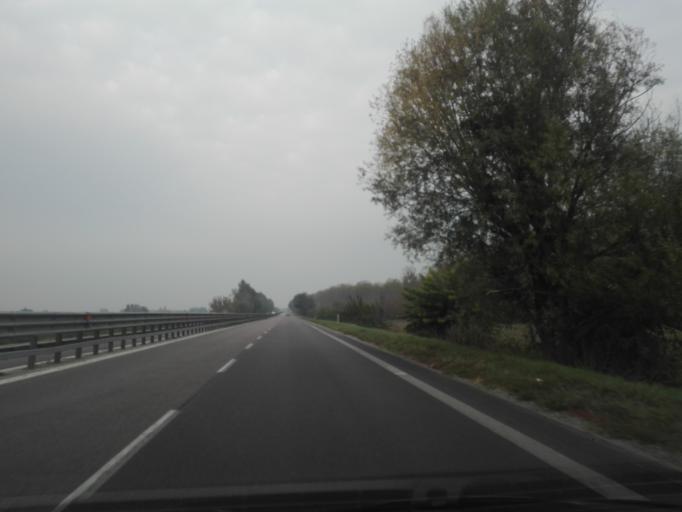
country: IT
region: Veneto
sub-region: Provincia di Verona
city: Spinimbecco
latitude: 45.1300
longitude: 11.3733
